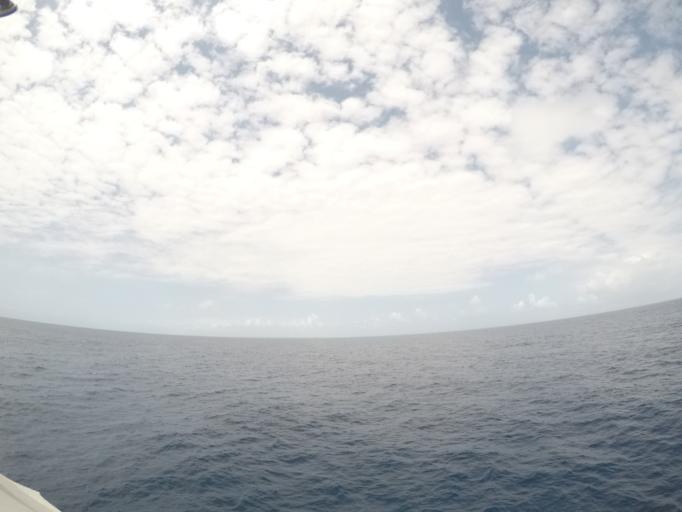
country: TZ
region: Zanzibar North
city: Nungwi
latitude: -5.6027
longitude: 39.3399
